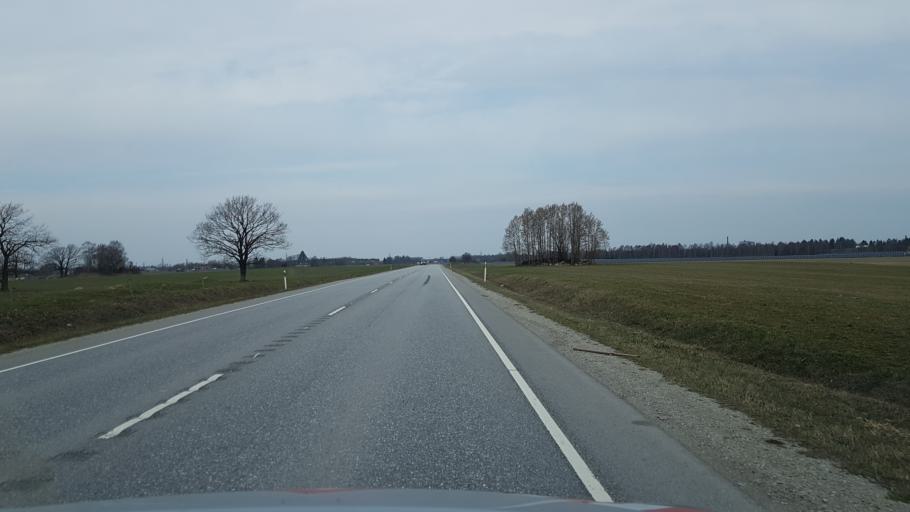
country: EE
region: Laeaene-Virumaa
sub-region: Someru vald
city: Someru
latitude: 59.3476
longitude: 26.4054
